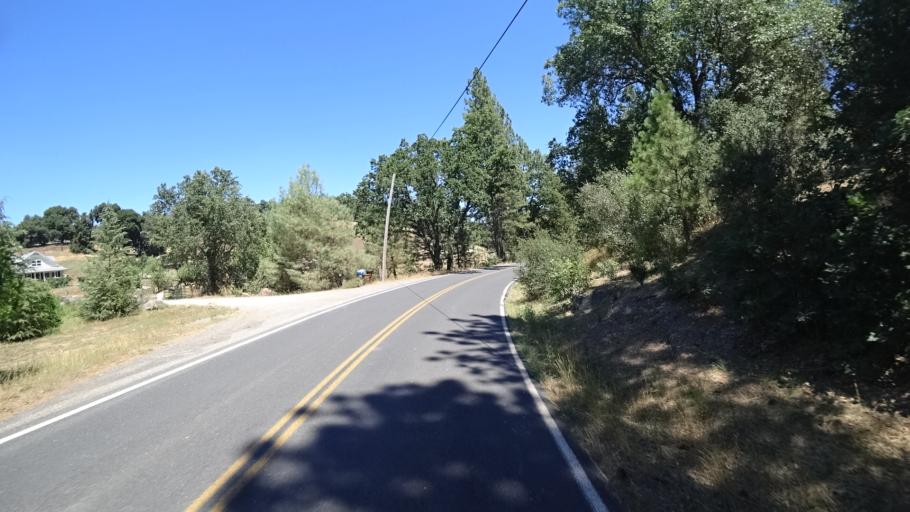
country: US
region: California
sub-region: Calaveras County
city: Mountain Ranch
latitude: 38.2867
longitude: -120.4989
